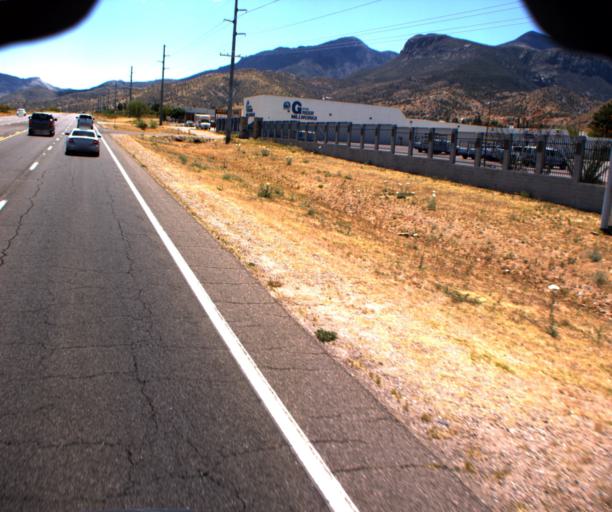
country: US
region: Arizona
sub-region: Cochise County
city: Sierra Vista Southeast
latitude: 31.4620
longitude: -110.2575
